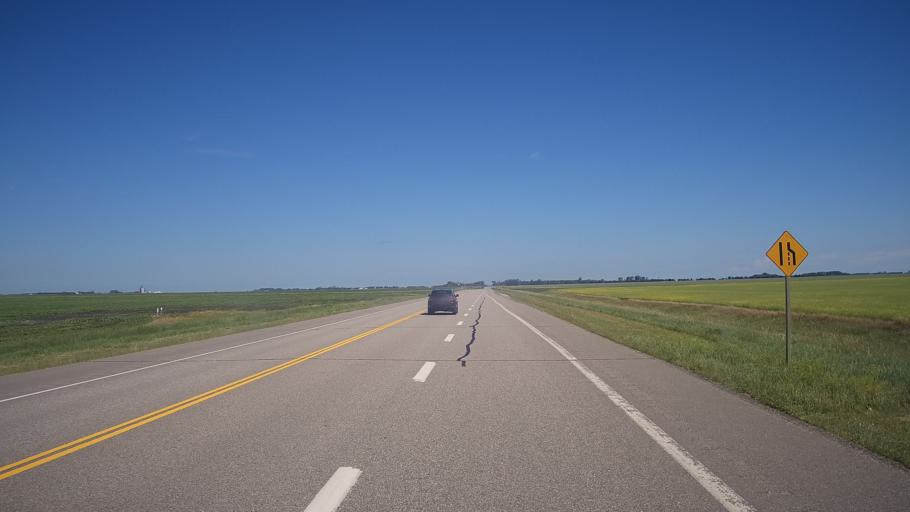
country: CA
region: Manitoba
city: Portage la Prairie
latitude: 50.0305
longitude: -98.4688
